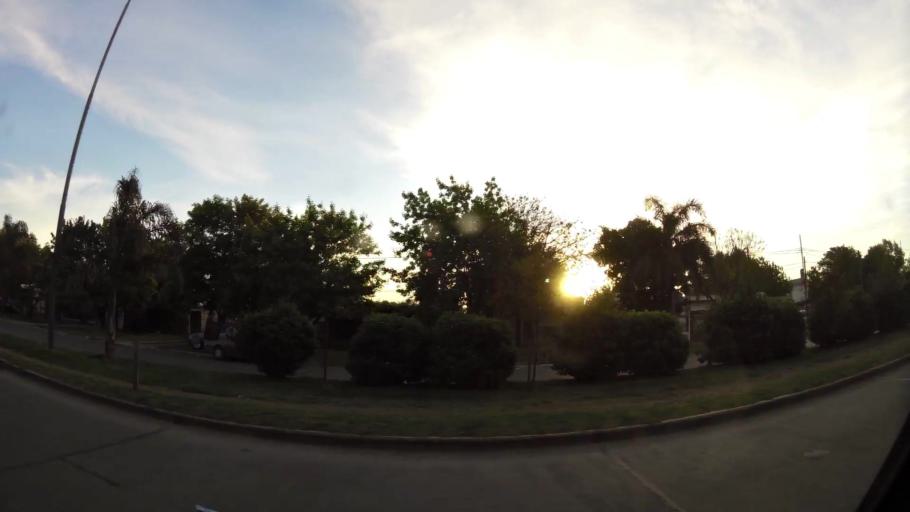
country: AR
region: Buenos Aires
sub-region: Partido de Quilmes
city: Quilmes
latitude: -34.7791
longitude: -58.2260
